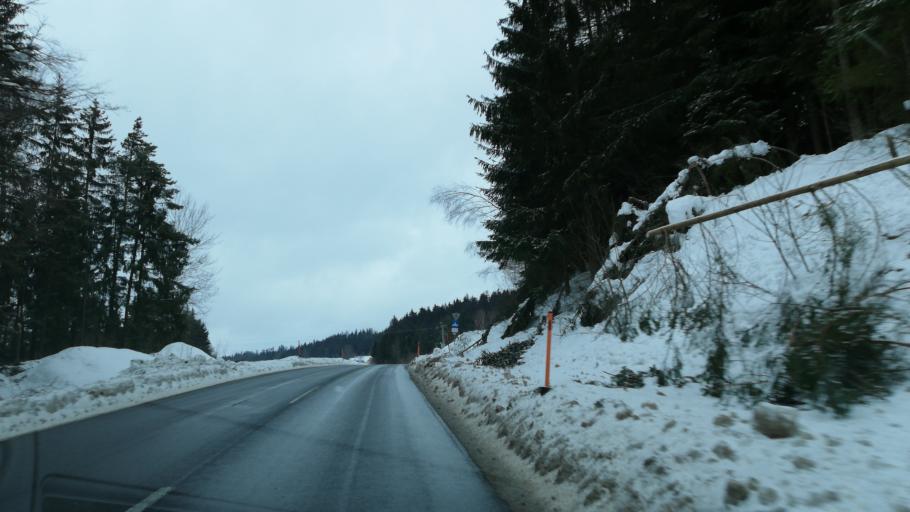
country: AT
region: Upper Austria
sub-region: Politischer Bezirk Urfahr-Umgebung
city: Herzogsdorf
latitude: 48.4701
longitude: 14.1396
